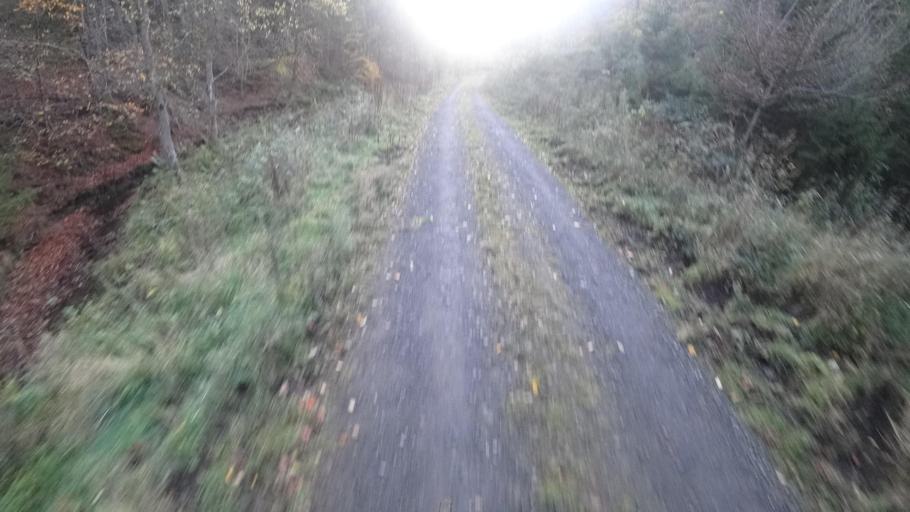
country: DE
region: Rheinland-Pfalz
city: Berg
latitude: 50.5302
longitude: 6.9652
